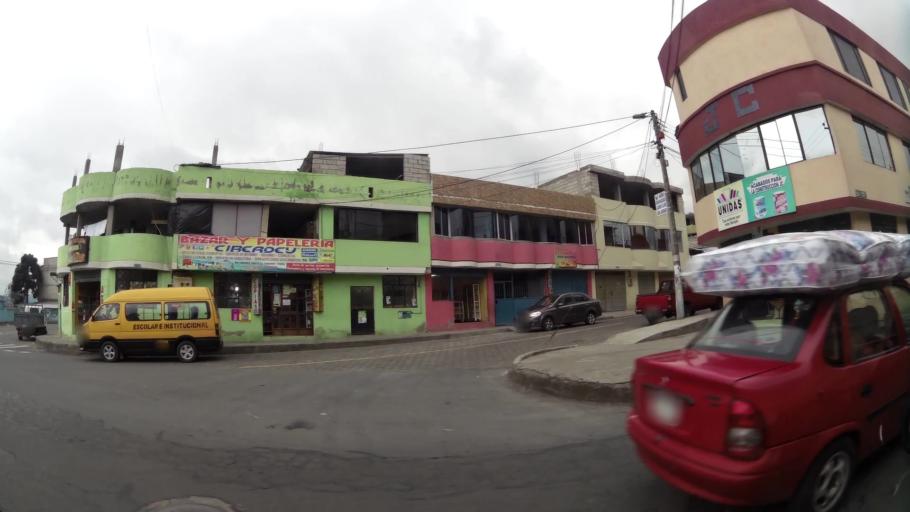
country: EC
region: Pichincha
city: Sangolqui
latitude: -0.3287
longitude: -78.5442
